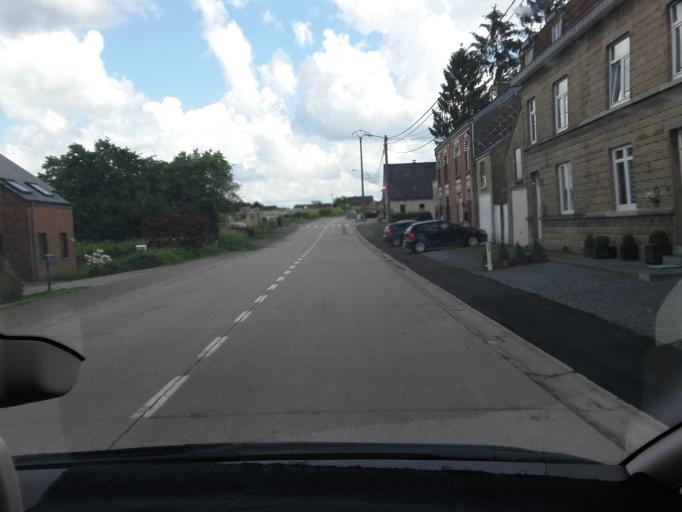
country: BE
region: Wallonia
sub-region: Province de Namur
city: Hamois
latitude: 50.2536
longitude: 5.1914
